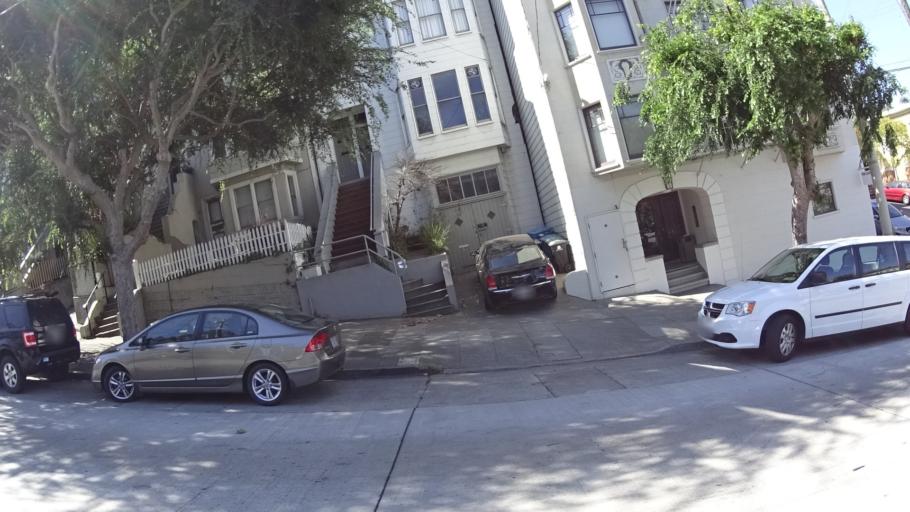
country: US
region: California
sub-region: San Francisco County
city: San Francisco
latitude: 37.7575
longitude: -122.4347
